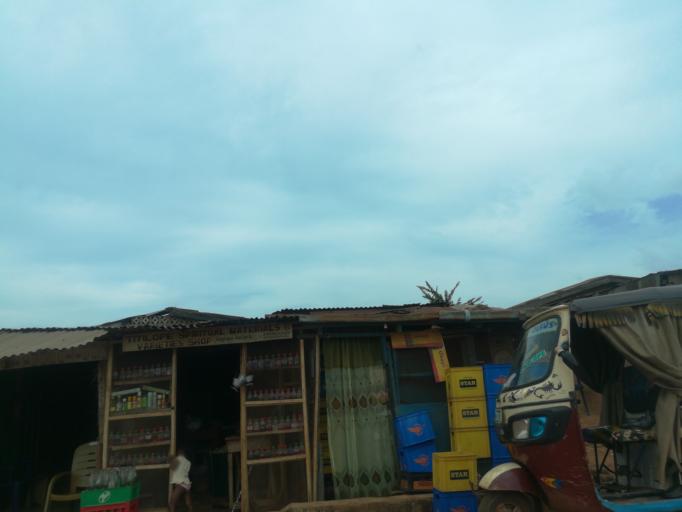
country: NG
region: Oyo
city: Ibadan
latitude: 7.3755
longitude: 3.9597
